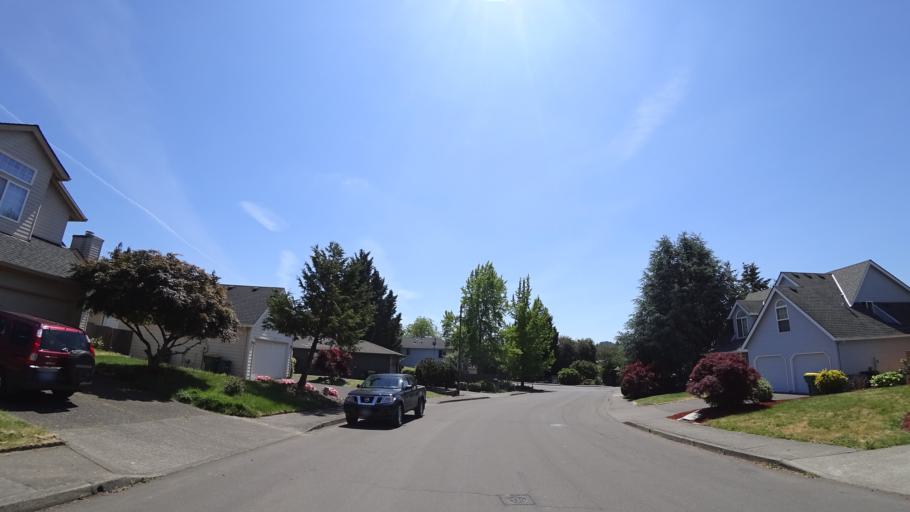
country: US
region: Oregon
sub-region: Washington County
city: Tigard
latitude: 45.4394
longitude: -122.8009
